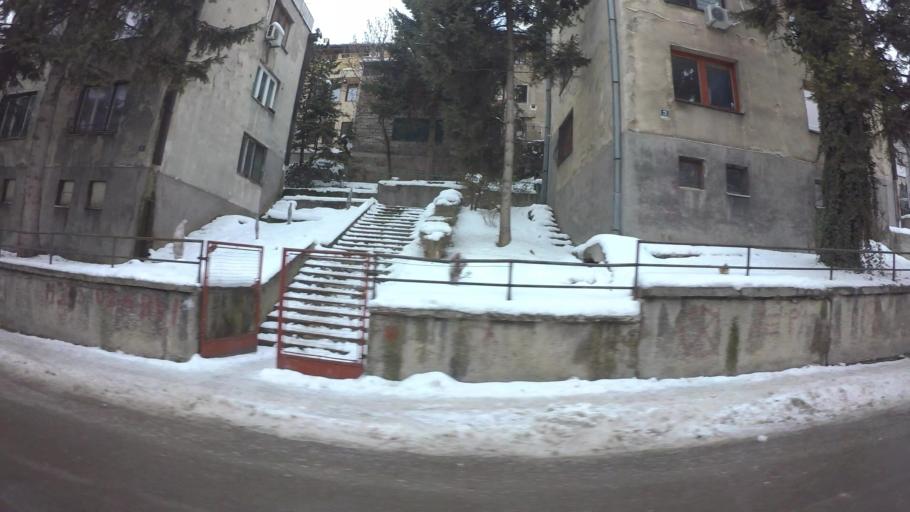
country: BA
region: Federation of Bosnia and Herzegovina
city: Kobilja Glava
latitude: 43.8623
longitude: 18.4313
